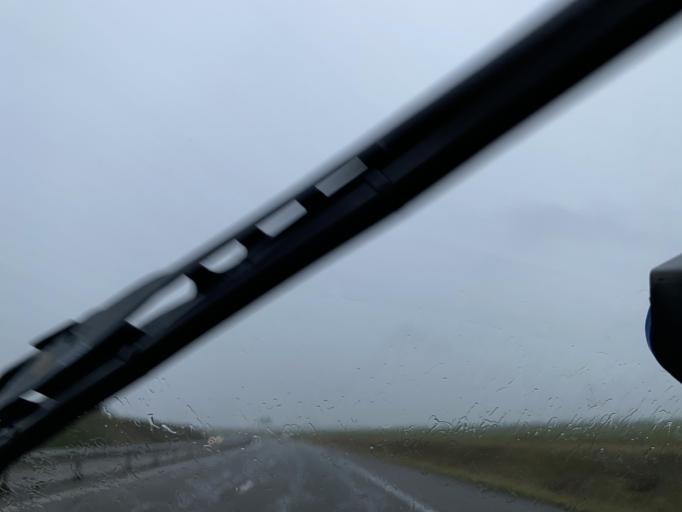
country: FR
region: Centre
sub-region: Departement d'Eure-et-Loir
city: Villemeux-sur-Eure
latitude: 48.6482
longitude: 1.3999
